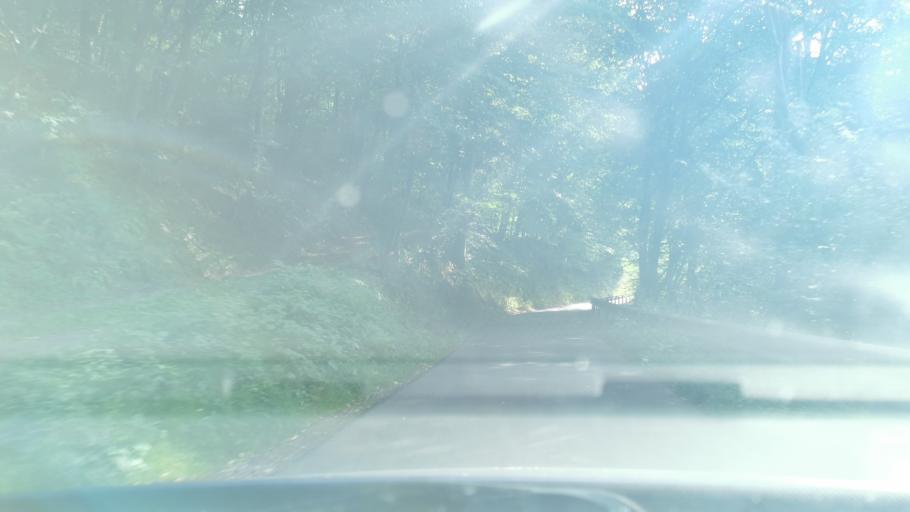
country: DE
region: Rheinland-Pfalz
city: Heckenmunster
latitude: 49.9082
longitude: 6.7834
